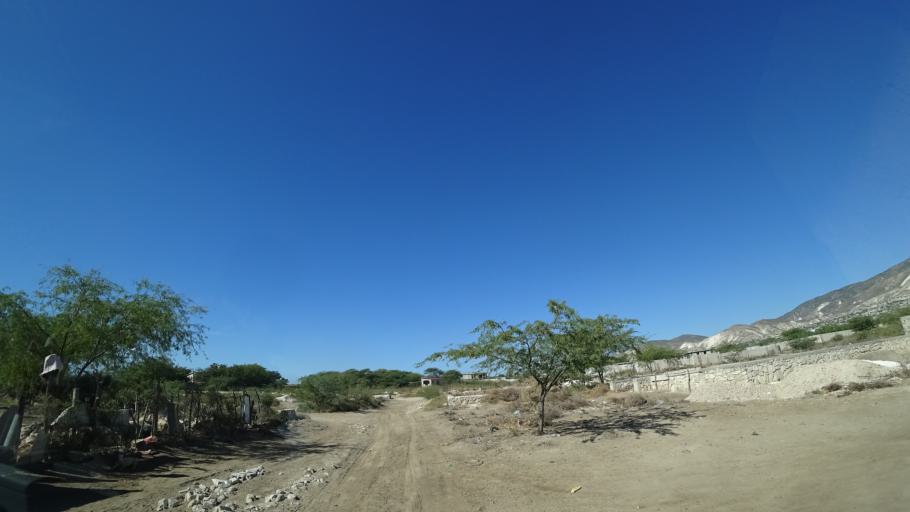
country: HT
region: Ouest
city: Croix des Bouquets
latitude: 18.6575
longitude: -72.2242
